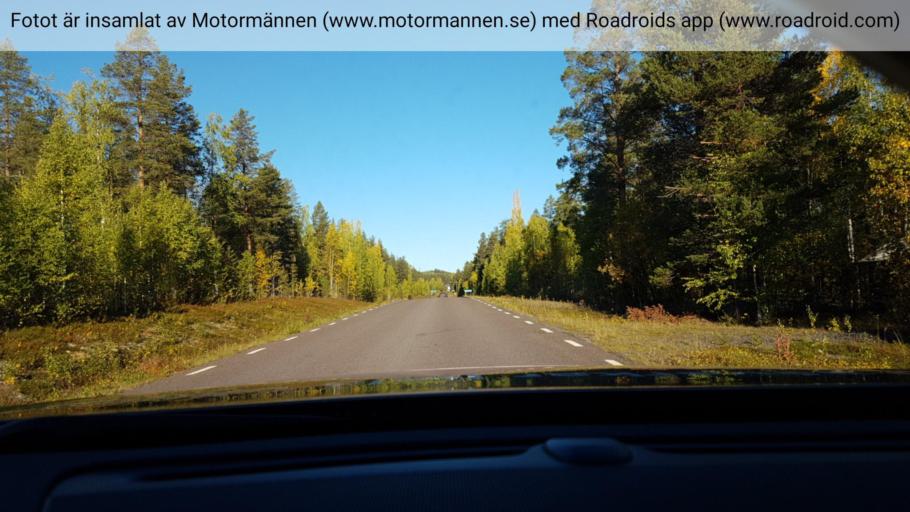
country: SE
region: Norrbotten
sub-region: Bodens Kommun
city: Boden
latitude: 66.1163
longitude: 21.3400
